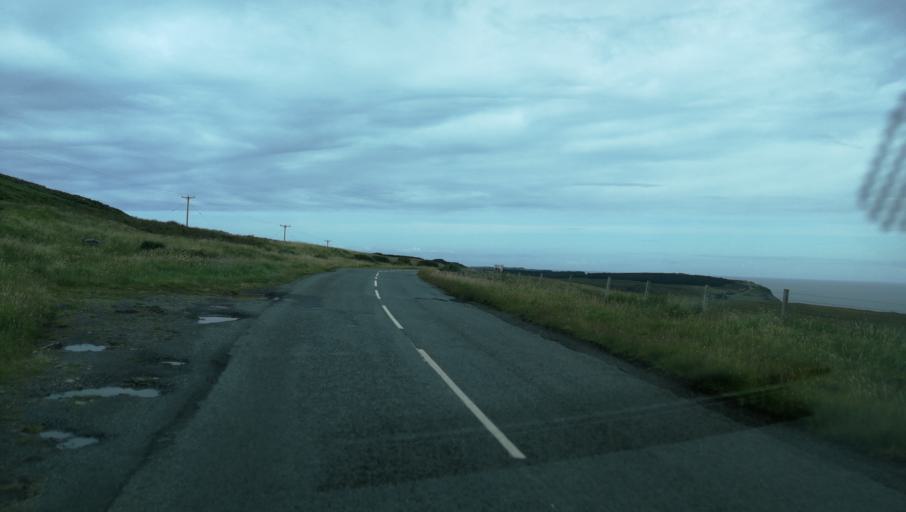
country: GB
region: Scotland
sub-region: Highland
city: Portree
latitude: 57.5171
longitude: -6.1528
